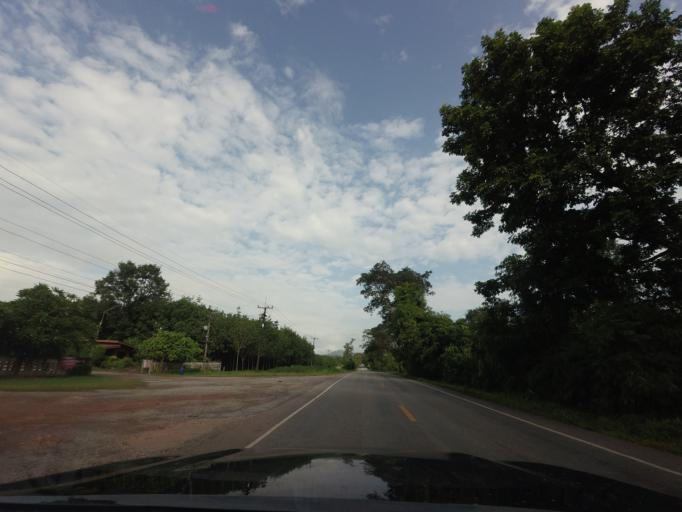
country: TH
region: Nong Khai
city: Pho Tak
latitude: 17.7917
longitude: 102.3586
